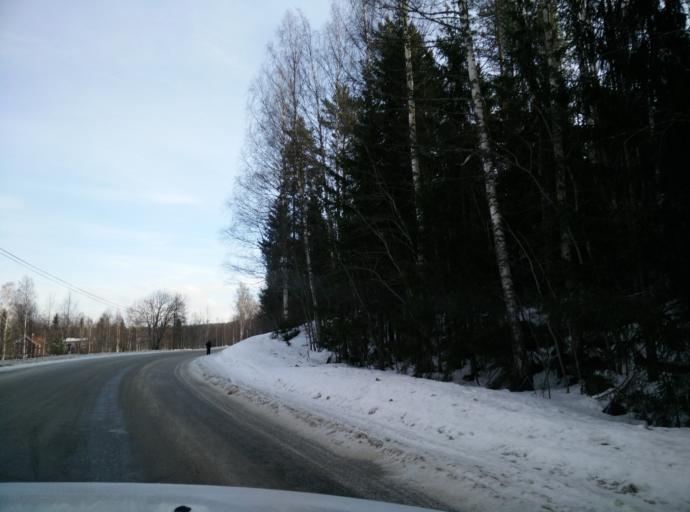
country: SE
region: Vaesternorrland
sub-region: Sundsvalls Kommun
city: Njurundabommen
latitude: 62.2015
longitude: 17.2721
